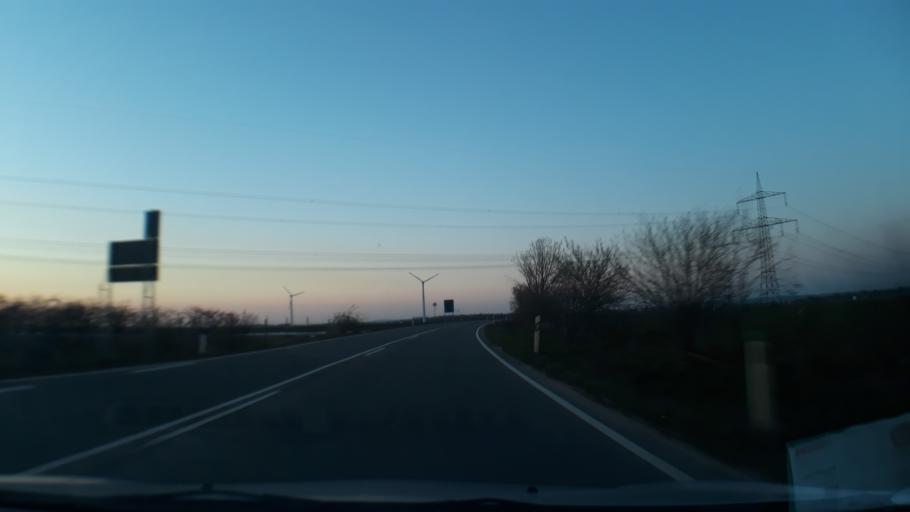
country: DE
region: North Rhine-Westphalia
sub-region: Regierungsbezirk Koln
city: Norvenich
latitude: 50.8544
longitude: 6.6133
